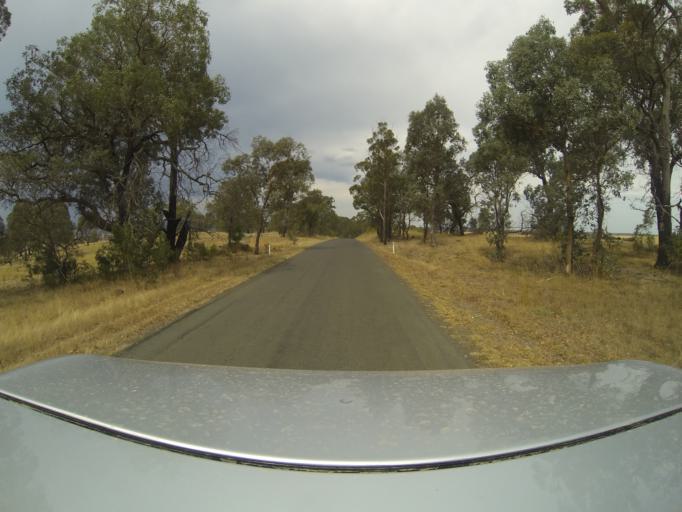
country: AU
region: Victoria
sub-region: Wellington
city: Heyfield
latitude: -37.9070
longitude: 146.7126
